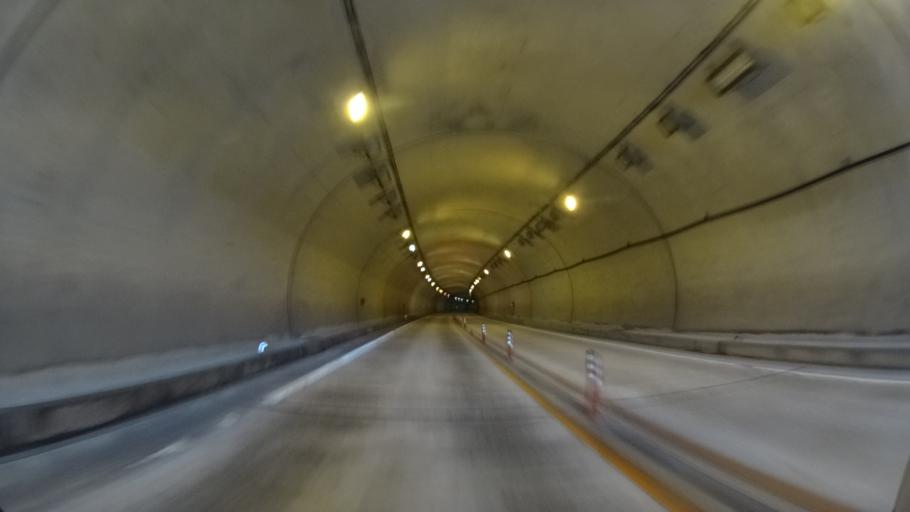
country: JP
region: Hyogo
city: Yamazakicho-nakabirose
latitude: 35.1067
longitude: 134.3304
